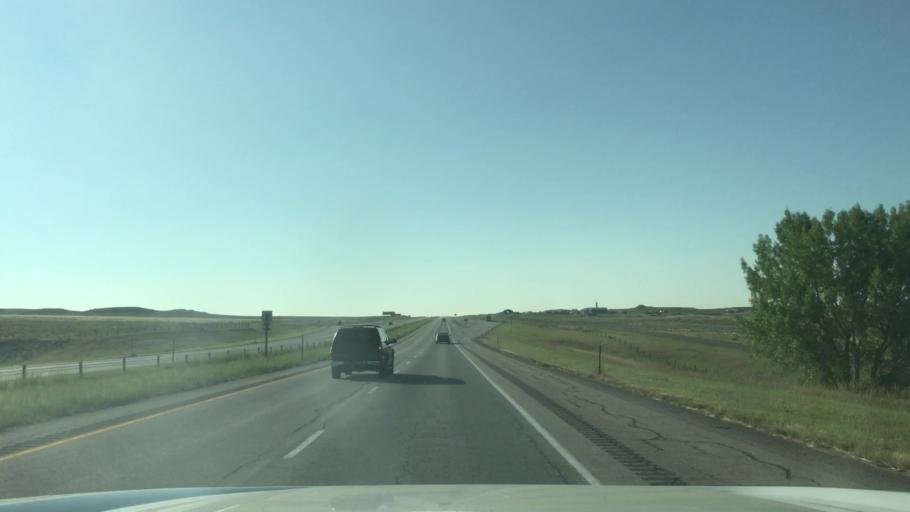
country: US
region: Wyoming
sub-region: Converse County
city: Douglas
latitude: 42.6886
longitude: -105.2402
